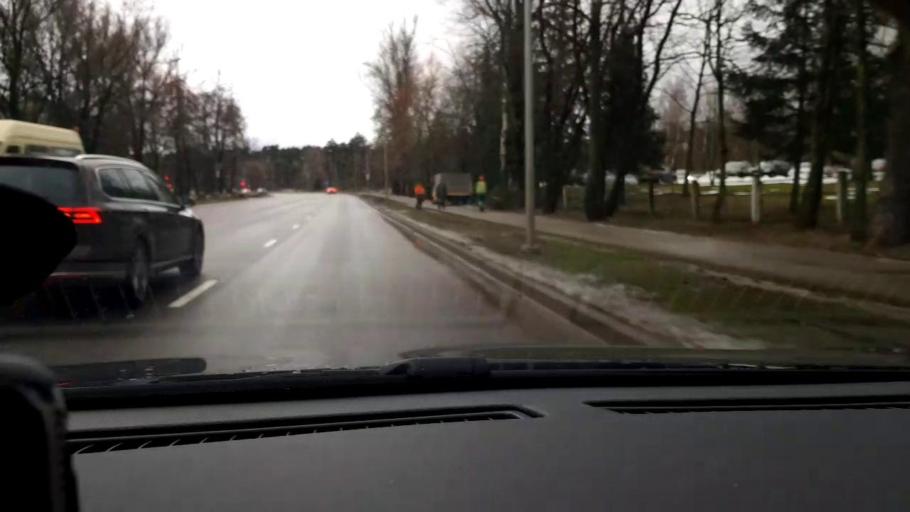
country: LT
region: Vilnius County
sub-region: Vilnius
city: Fabijoniskes
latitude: 54.7515
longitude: 25.2753
